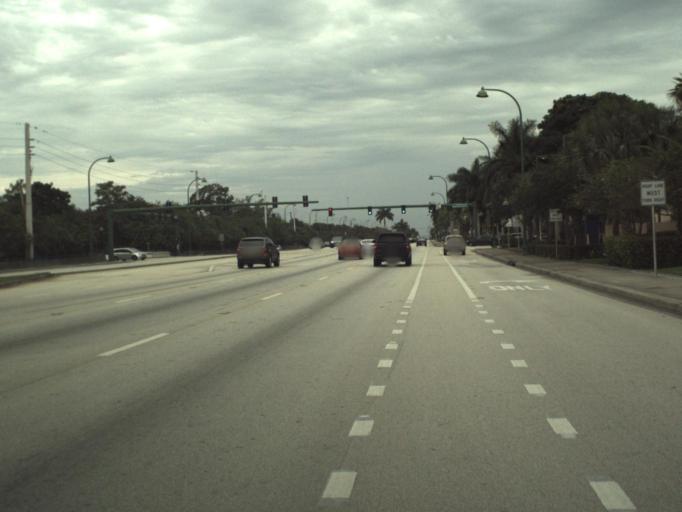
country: US
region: Florida
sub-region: Palm Beach County
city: Wellington
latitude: 26.6813
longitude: -80.2288
